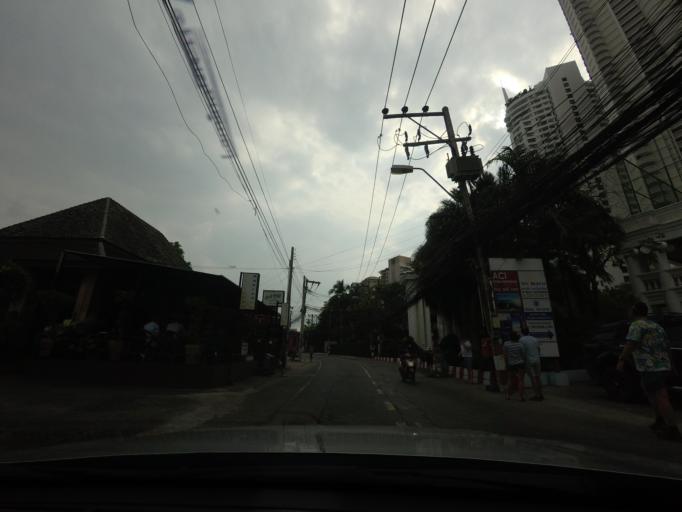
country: TH
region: Chon Buri
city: Phatthaya
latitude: 12.9611
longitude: 100.8868
